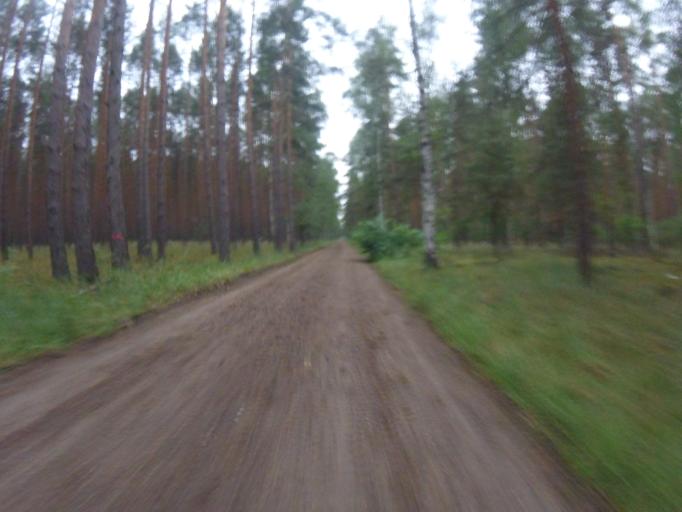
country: DE
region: Brandenburg
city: Gross Koris
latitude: 52.2025
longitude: 13.6978
